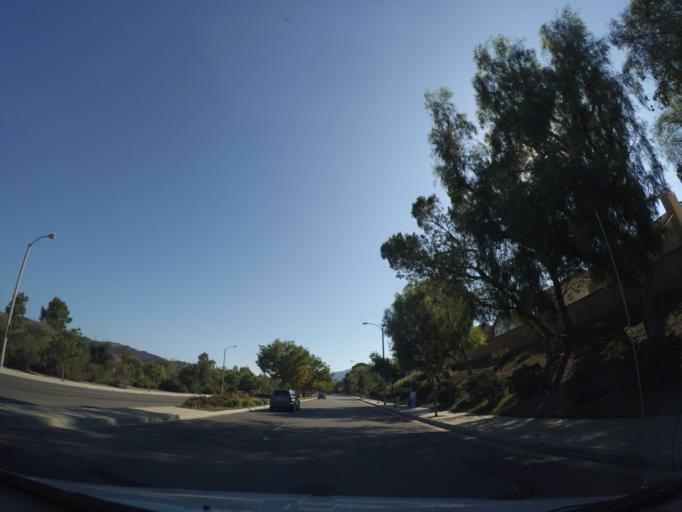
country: US
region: California
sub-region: Los Angeles County
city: Agoura
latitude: 34.1327
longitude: -118.7076
